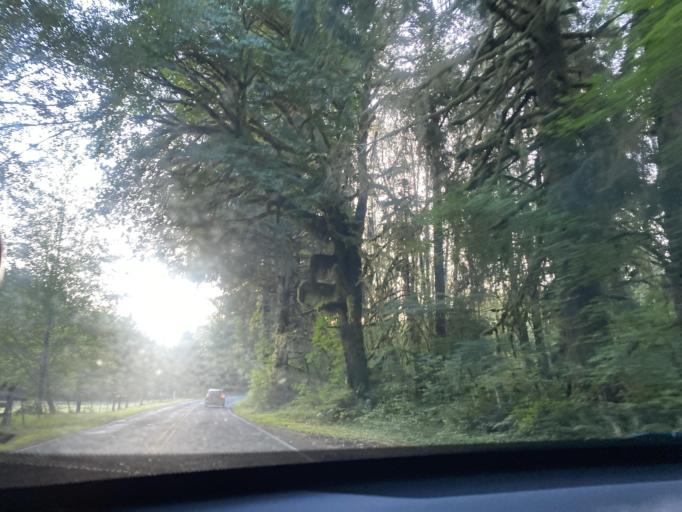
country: US
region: Washington
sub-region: Clallam County
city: Forks
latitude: 47.8161
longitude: -124.1668
